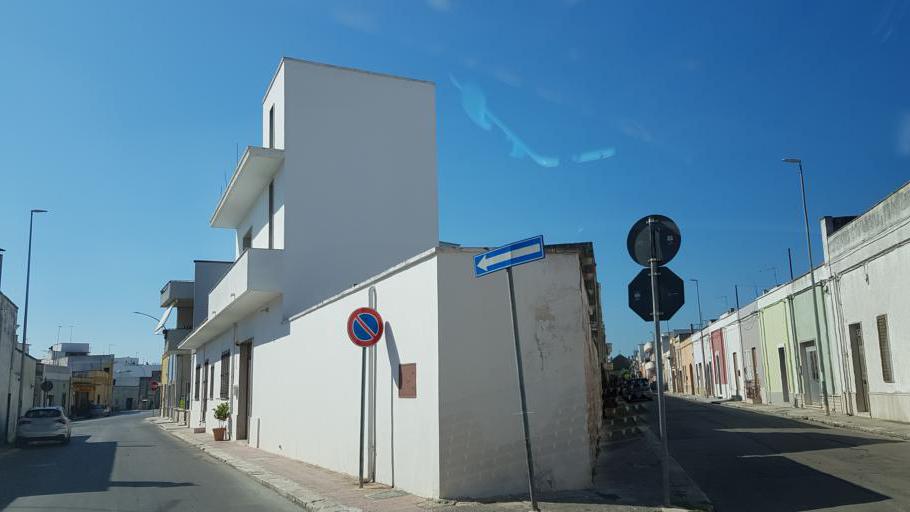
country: IT
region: Apulia
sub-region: Provincia di Brindisi
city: San Donaci
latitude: 40.4458
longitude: 17.9249
